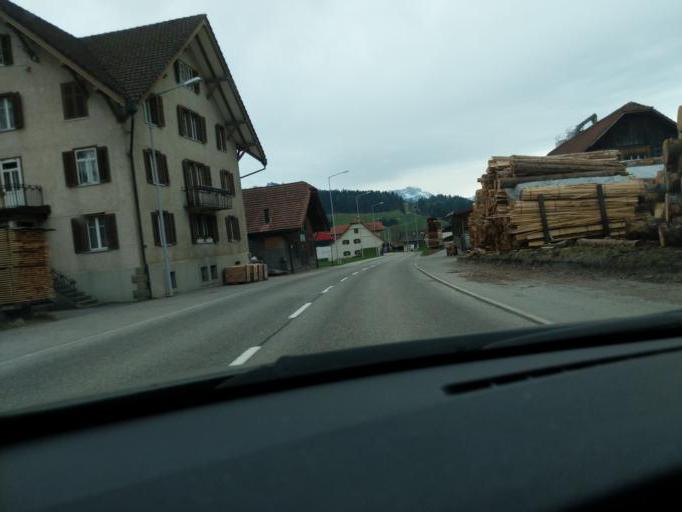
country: CH
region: Lucerne
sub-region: Entlebuch District
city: Escholzmatt
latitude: 46.9110
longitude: 7.9327
